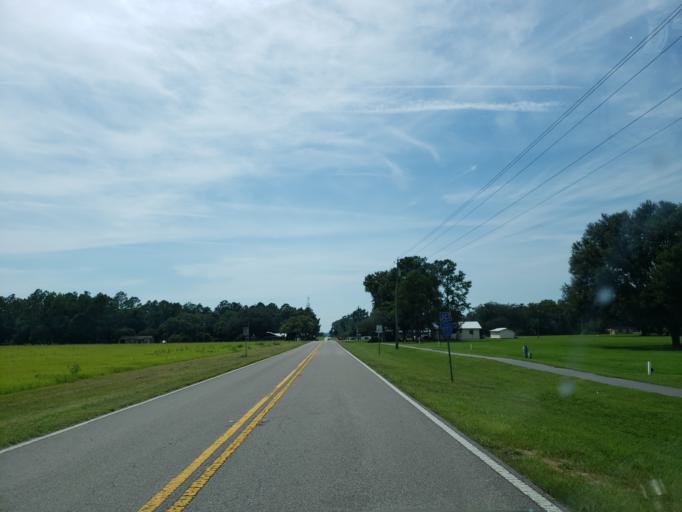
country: US
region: Florida
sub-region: Pasco County
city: San Antonio
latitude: 28.3760
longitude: -82.2846
